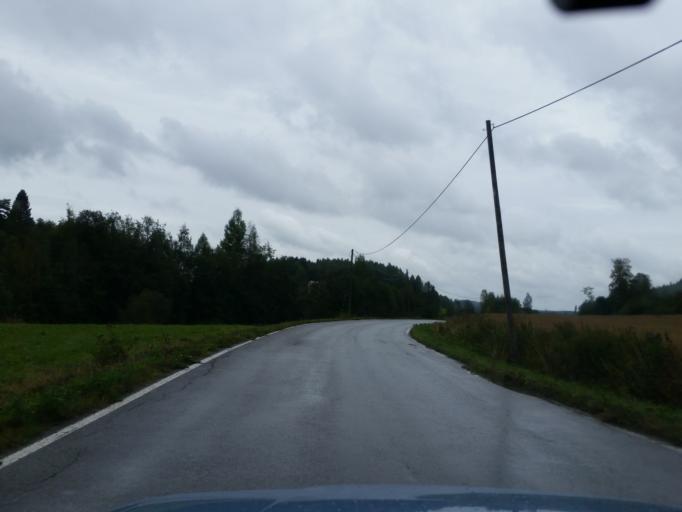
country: FI
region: Uusimaa
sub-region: Helsinki
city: Sammatti
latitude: 60.4391
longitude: 23.8414
